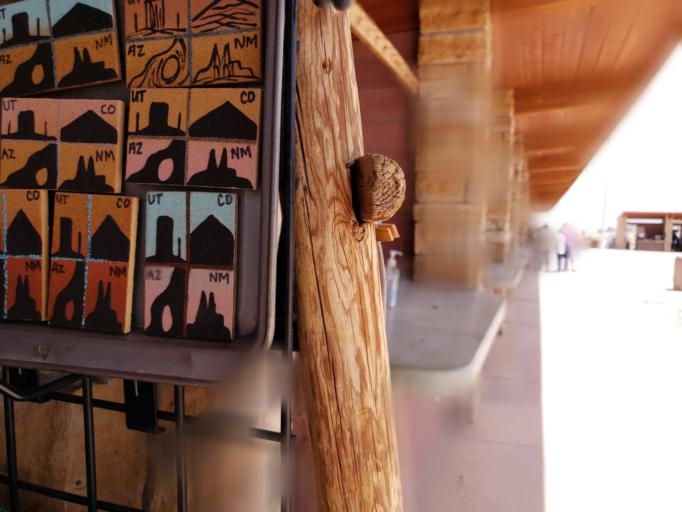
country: US
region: Colorado
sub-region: Montezuma County
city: Towaoc
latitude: 36.9993
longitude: -109.0451
